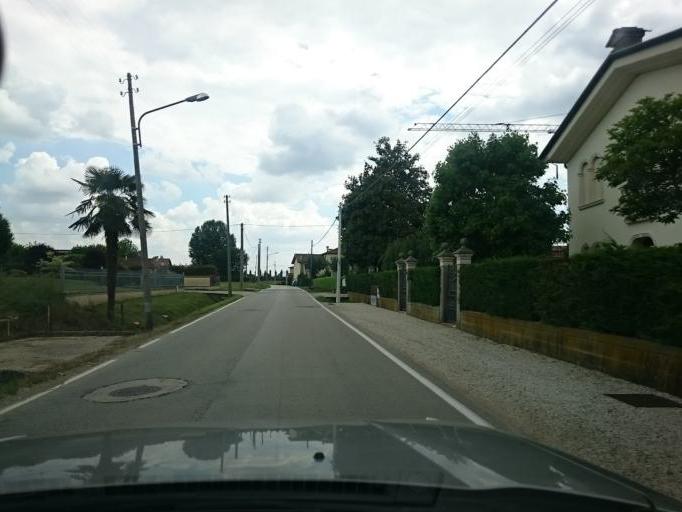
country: IT
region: Veneto
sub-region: Provincia di Vicenza
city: Arcugnano-Torri
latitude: 45.5212
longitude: 11.5802
